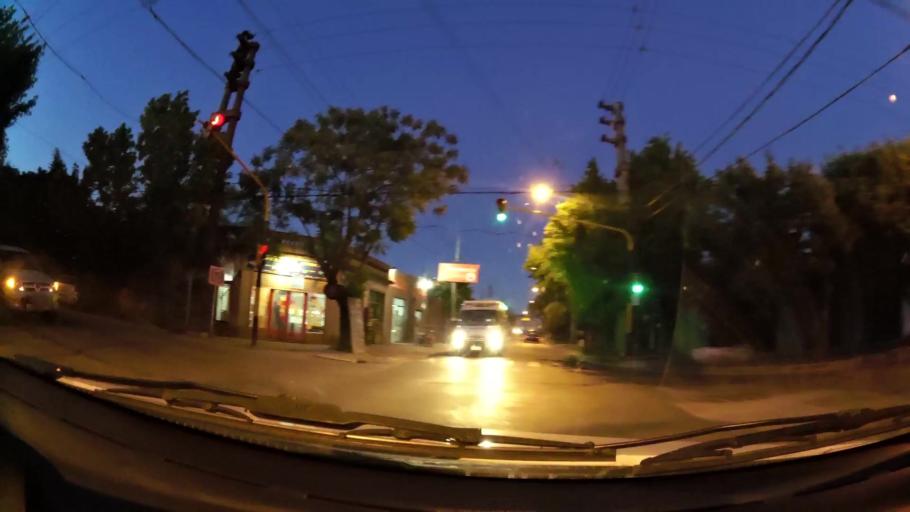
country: AR
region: Buenos Aires
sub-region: Partido de Quilmes
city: Quilmes
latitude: -34.7798
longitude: -58.1793
